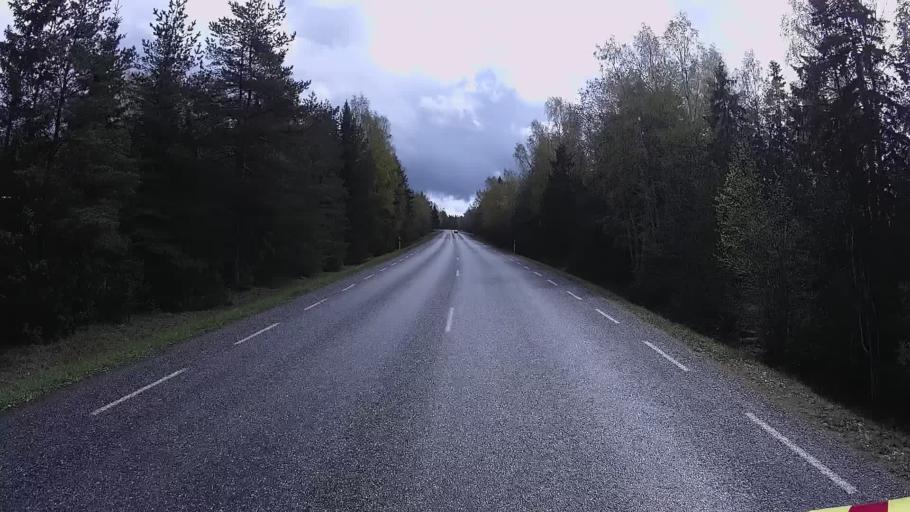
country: EE
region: Hiiumaa
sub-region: Kaerdla linn
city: Kardla
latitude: 58.9779
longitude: 22.8125
